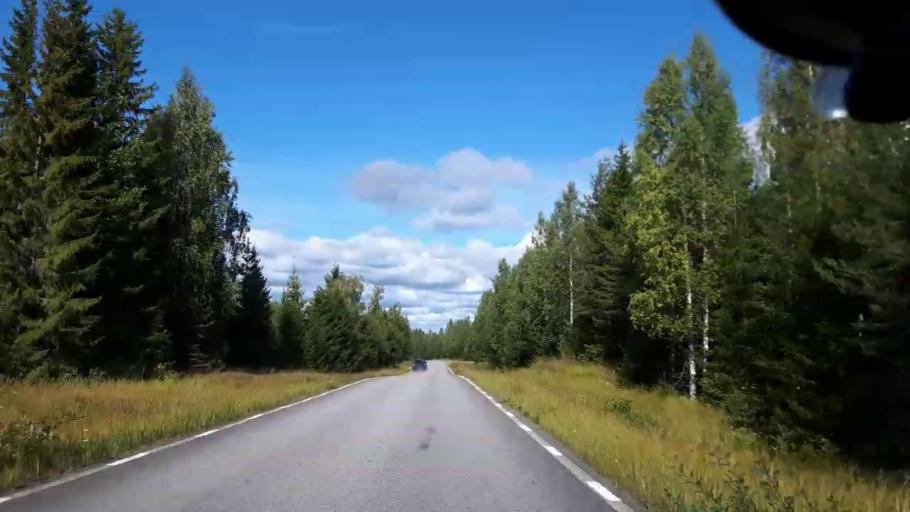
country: SE
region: Jaemtland
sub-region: OEstersunds Kommun
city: Brunflo
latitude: 63.2123
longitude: 15.2480
